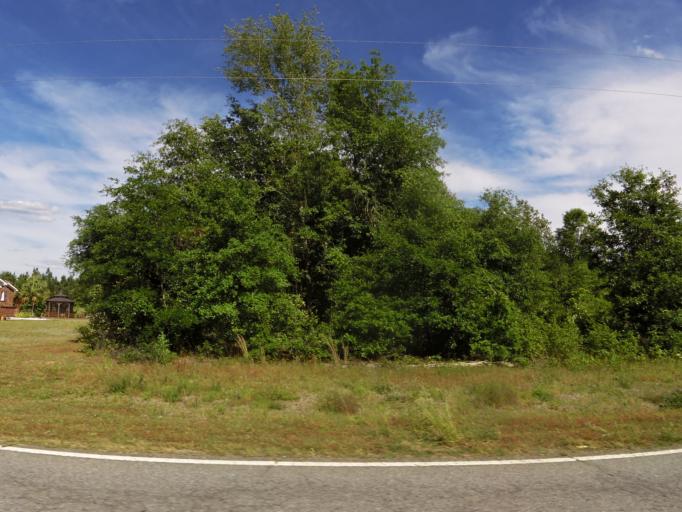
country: US
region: South Carolina
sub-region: Bamberg County
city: Denmark
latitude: 33.2022
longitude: -81.1771
